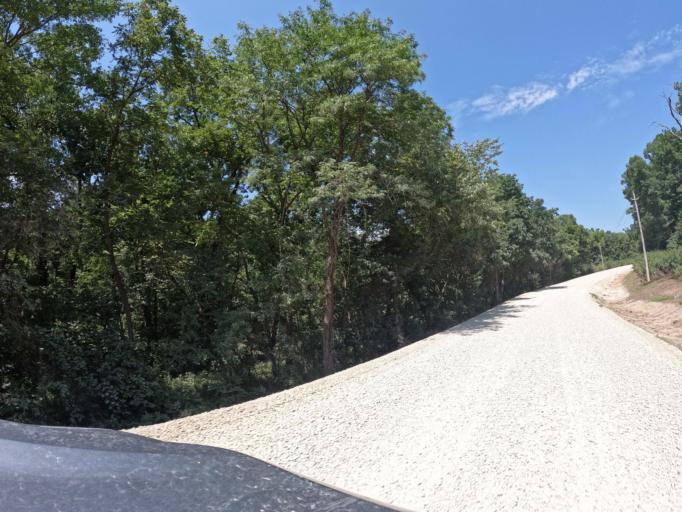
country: US
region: Iowa
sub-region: Henry County
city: Mount Pleasant
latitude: 40.9041
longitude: -91.6798
